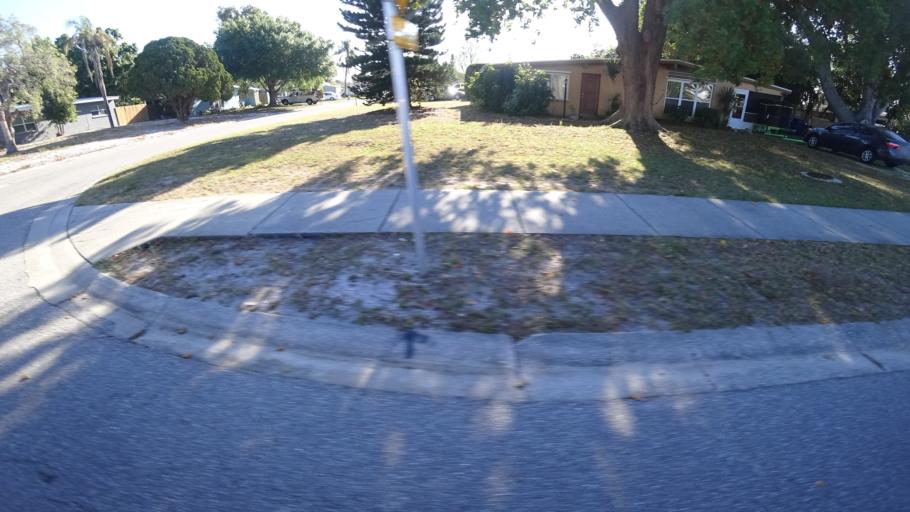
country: US
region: Florida
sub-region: Manatee County
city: Bayshore Gardens
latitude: 27.4220
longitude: -82.5878
